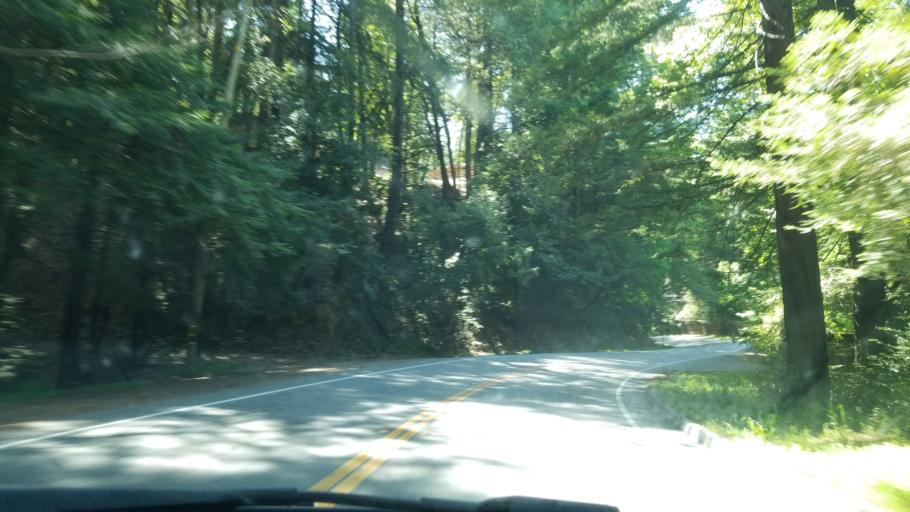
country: US
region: California
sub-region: Santa Clara County
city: Lexington Hills
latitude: 37.1159
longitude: -121.9340
